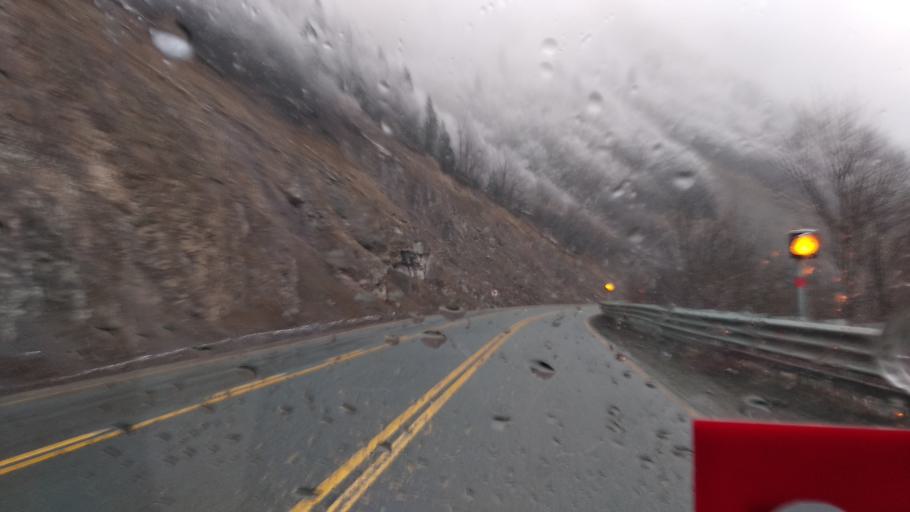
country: TR
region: Trabzon
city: Macka
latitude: 40.7009
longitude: 39.4853
